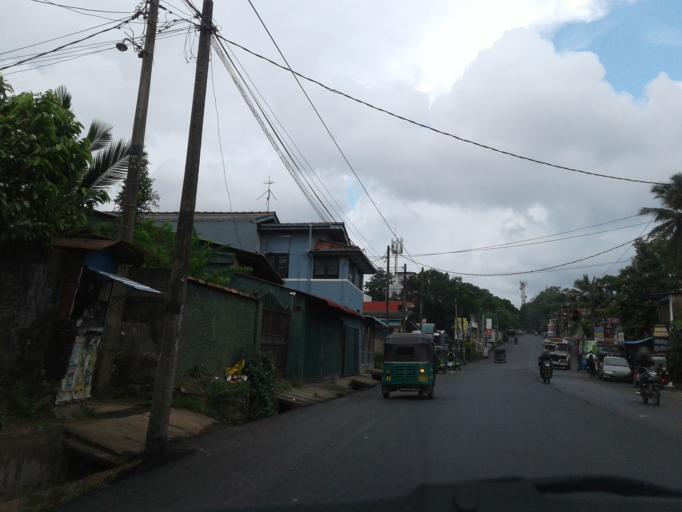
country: LK
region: Western
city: Moratuwa
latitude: 6.7963
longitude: 79.8962
